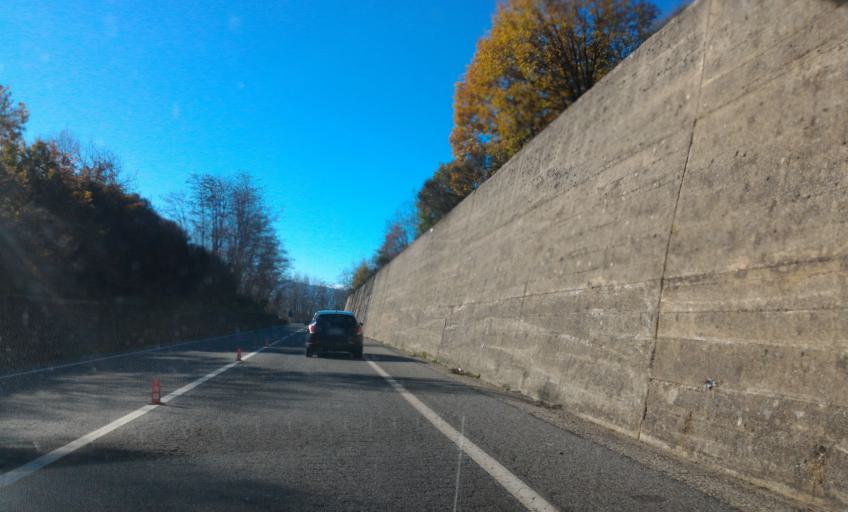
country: IT
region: Calabria
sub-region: Provincia di Cosenza
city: Celico
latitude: 39.3161
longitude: 16.3342
